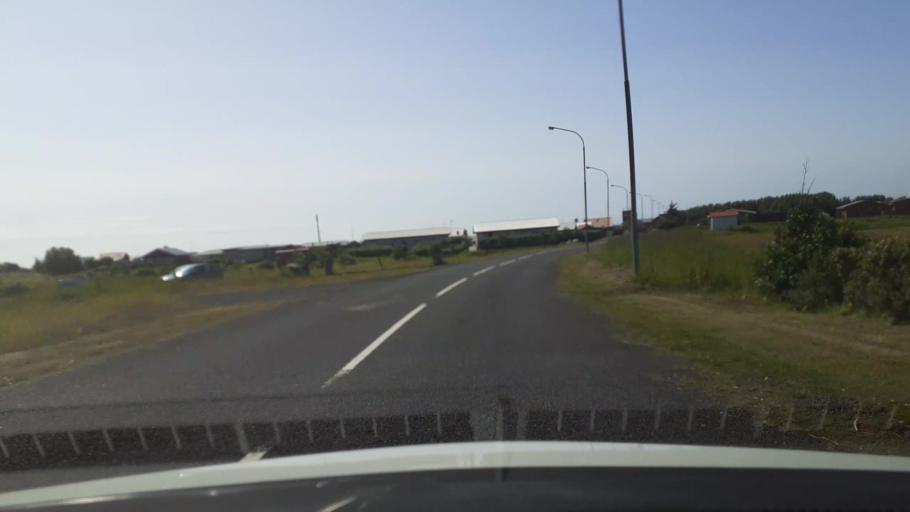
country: IS
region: South
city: Selfoss
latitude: 63.8398
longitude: -21.0550
